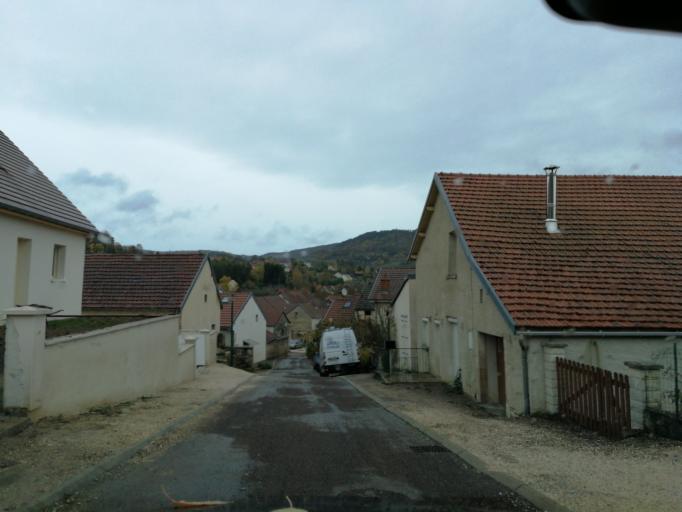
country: FR
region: Bourgogne
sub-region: Departement de la Cote-d'Or
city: Fleurey-sur-Ouche
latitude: 47.3217
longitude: 4.7919
